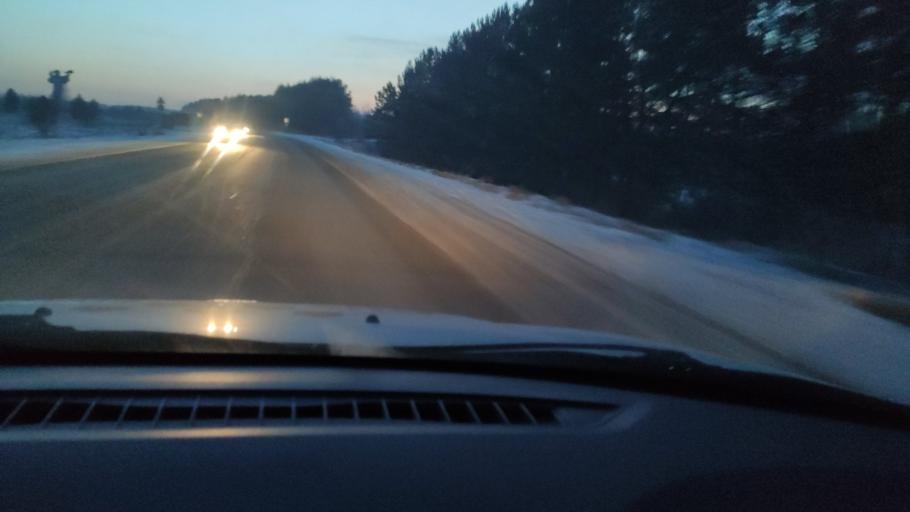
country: RU
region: Perm
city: Kungur
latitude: 57.4210
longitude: 56.9221
